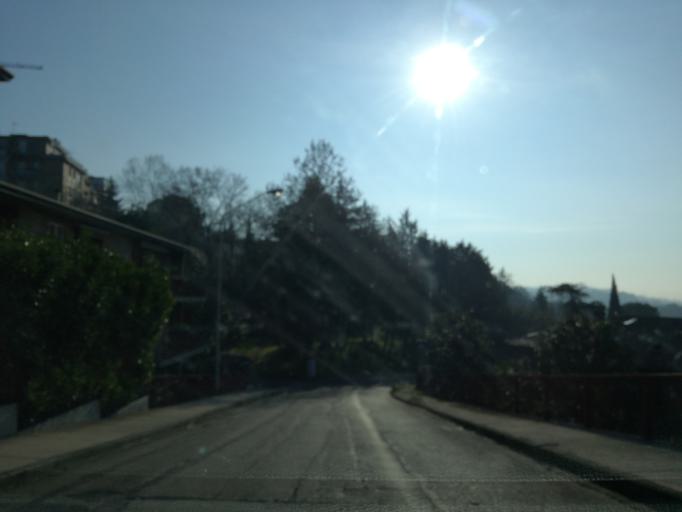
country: IT
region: Umbria
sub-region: Provincia di Perugia
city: Perugia
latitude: 43.1100
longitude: 12.3709
